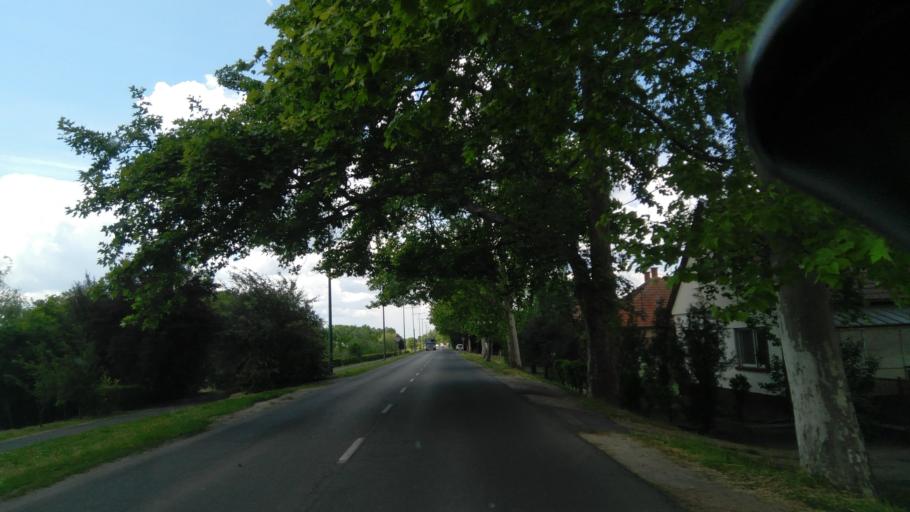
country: HU
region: Bekes
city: Gyula
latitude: 46.6473
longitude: 21.2522
